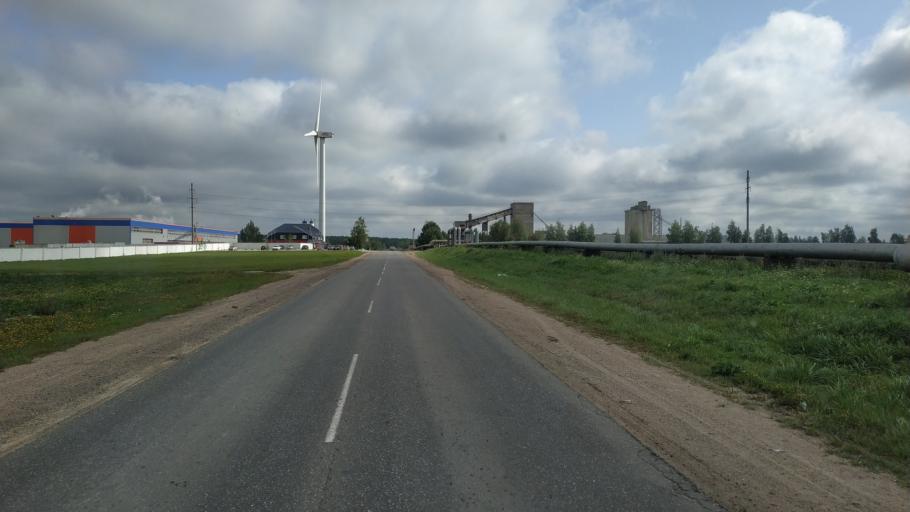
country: BY
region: Mogilev
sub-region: Mahilyowski Rayon
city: Veyno
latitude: 53.8391
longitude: 30.3750
